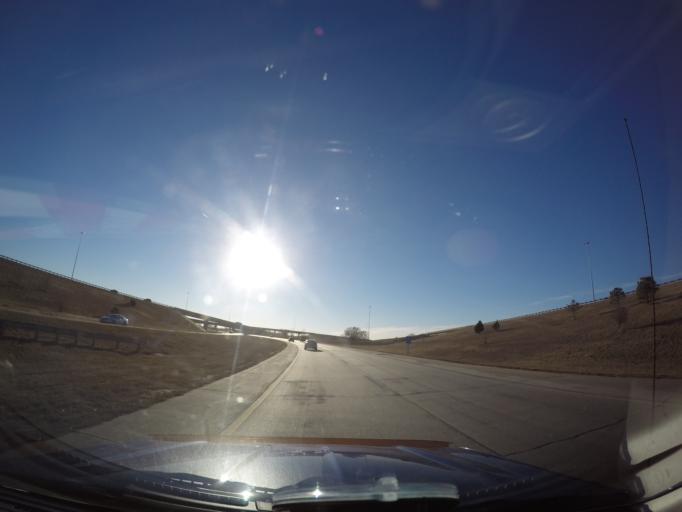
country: US
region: Kansas
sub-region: Sedgwick County
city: Park City
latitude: 37.7572
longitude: -97.3714
